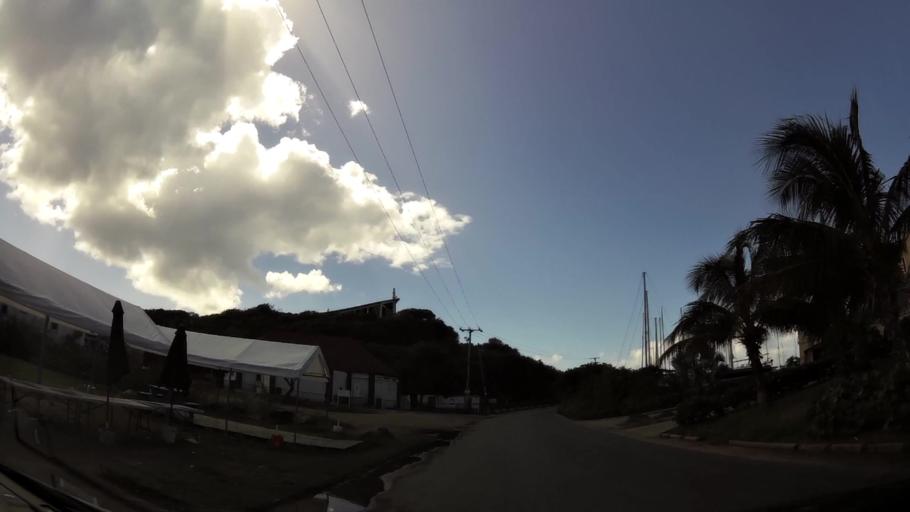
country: VG
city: Tortola
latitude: 18.4476
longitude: -64.4361
